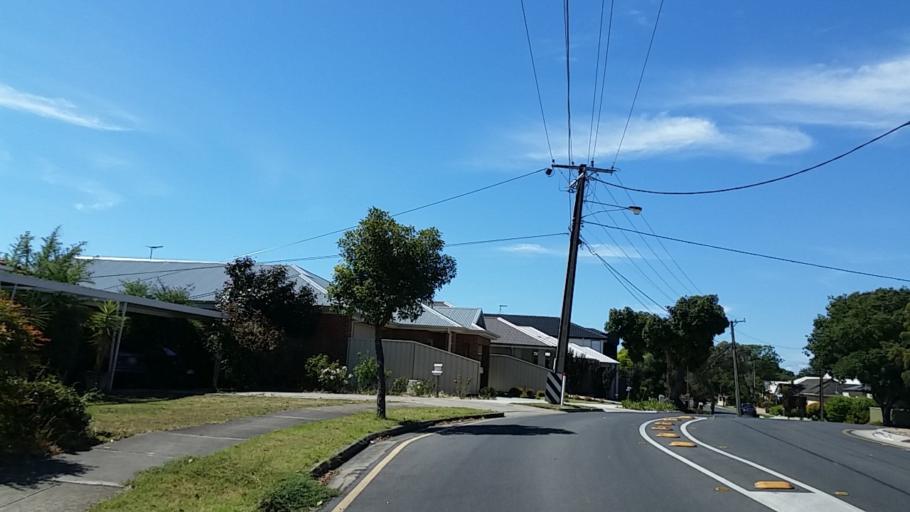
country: AU
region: South Australia
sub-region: Charles Sturt
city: Findon
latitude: -34.9249
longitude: 138.5275
